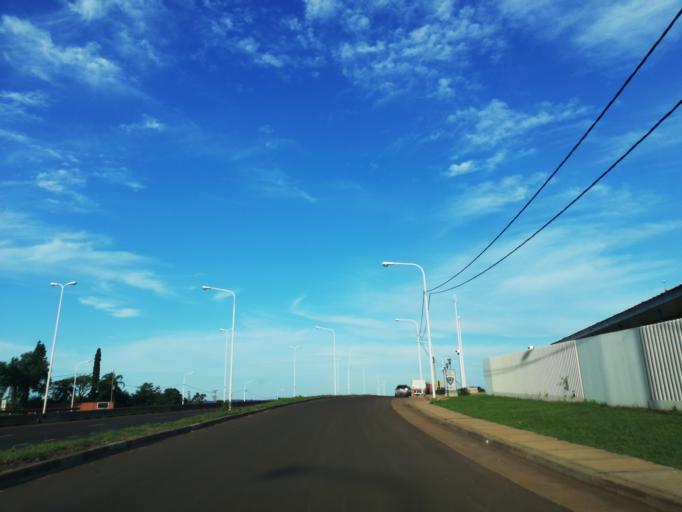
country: AR
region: Misiones
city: Garupa
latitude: -27.4527
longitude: -55.8598
